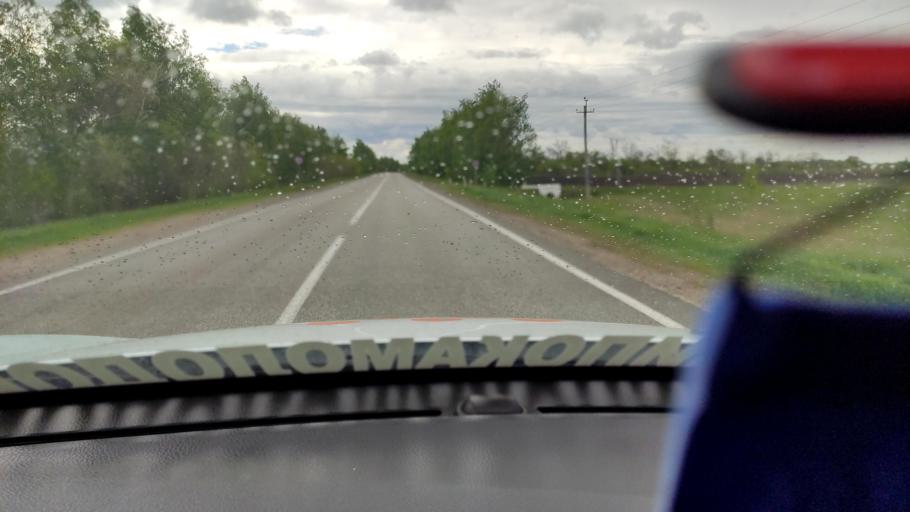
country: RU
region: Voronezj
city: Imeni Pervogo Maya
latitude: 50.7682
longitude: 39.3879
